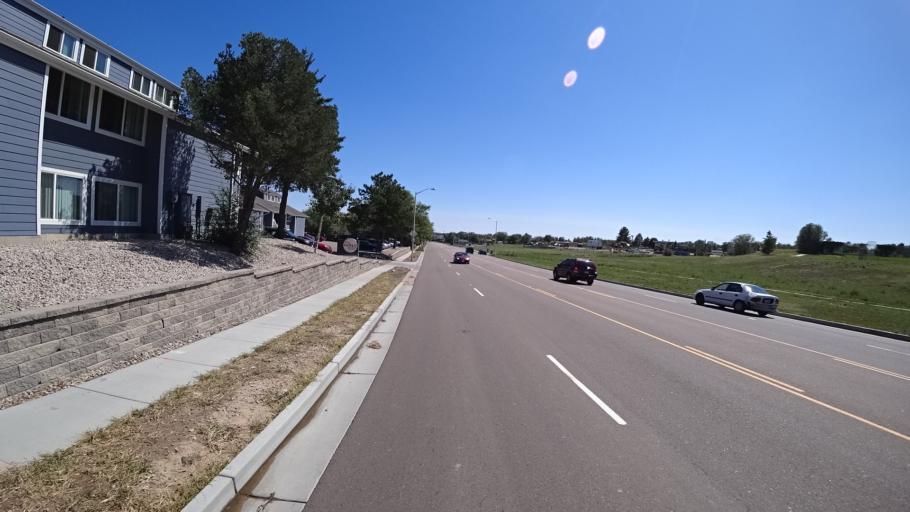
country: US
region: Colorado
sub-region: El Paso County
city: Stratmoor
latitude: 38.8096
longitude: -104.7659
